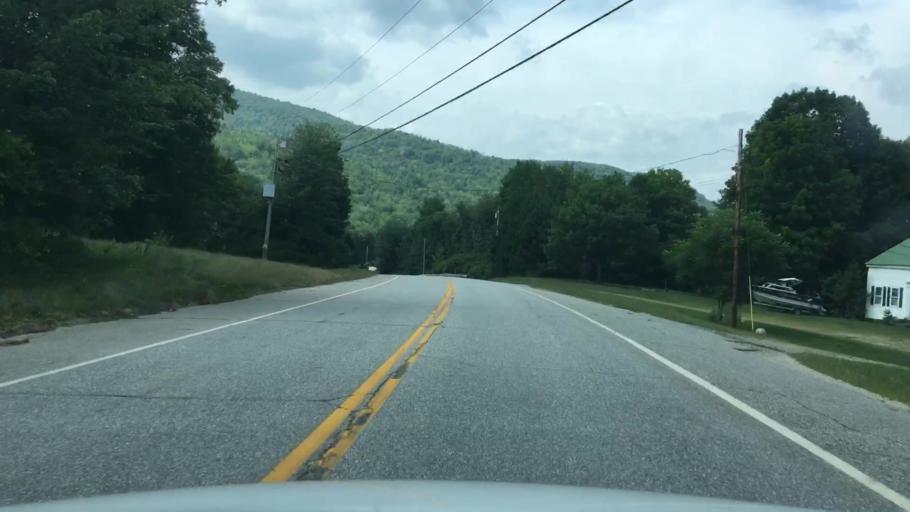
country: US
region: Maine
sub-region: Oxford County
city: Rumford
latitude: 44.5482
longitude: -70.7015
